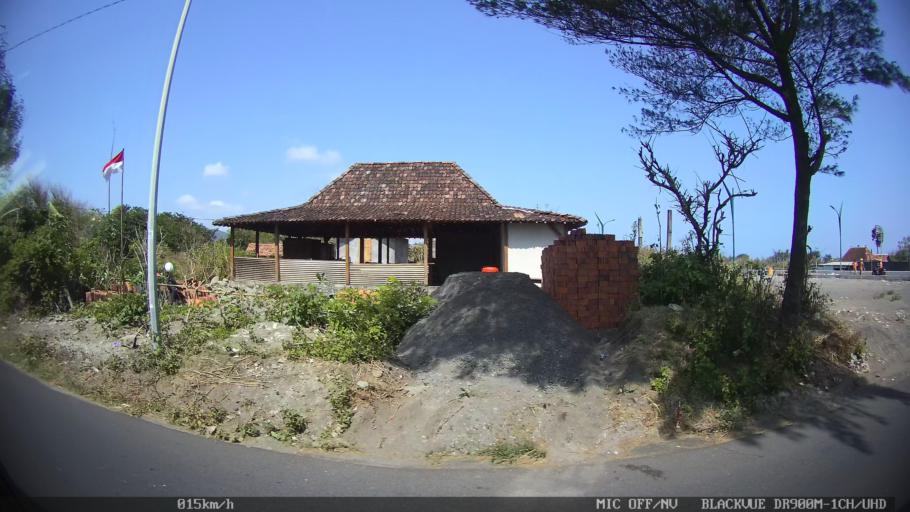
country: ID
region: Daerah Istimewa Yogyakarta
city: Bambanglipuro
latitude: -8.0108
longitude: 110.2948
